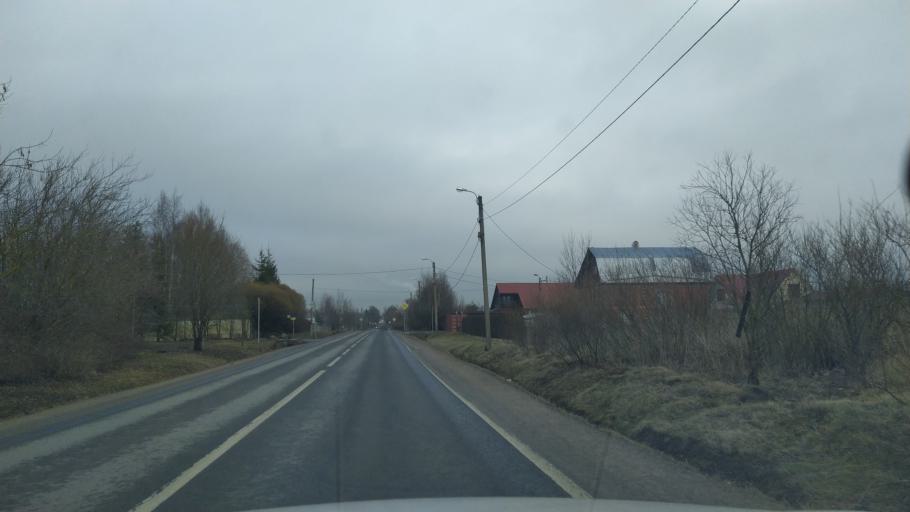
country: RU
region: St.-Petersburg
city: Aleksandrovskaya
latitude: 59.7222
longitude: 30.3461
